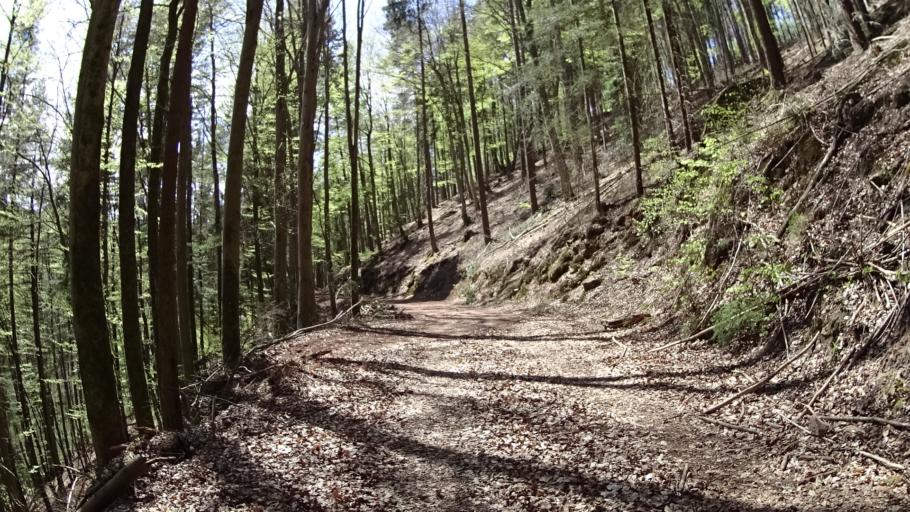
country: DE
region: Rheinland-Pfalz
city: Ramberg
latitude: 49.3041
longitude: 7.9989
